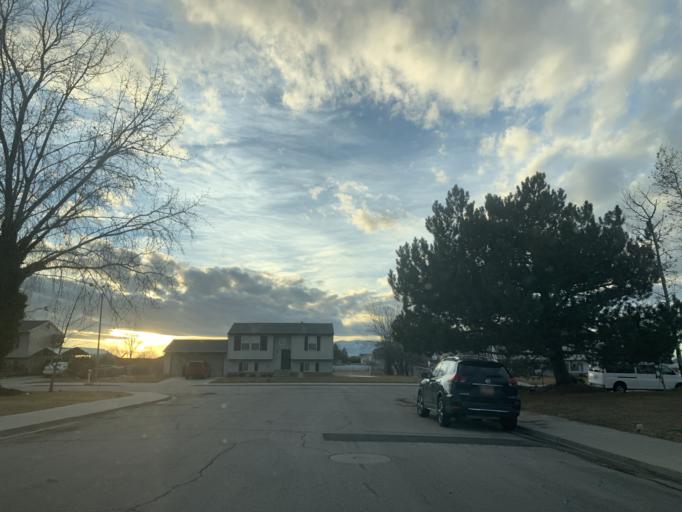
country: US
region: Utah
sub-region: Utah County
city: Provo
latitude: 40.2442
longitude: -111.7031
